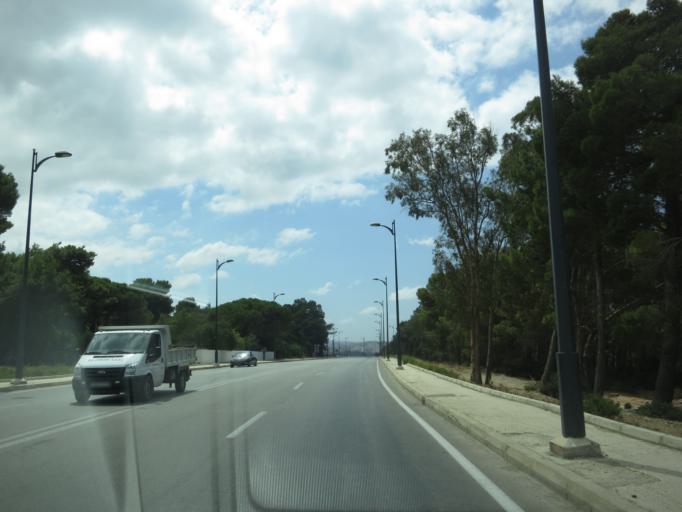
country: MA
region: Tanger-Tetouan
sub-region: Tanger-Assilah
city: Tangier
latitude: 35.7946
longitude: -5.7484
